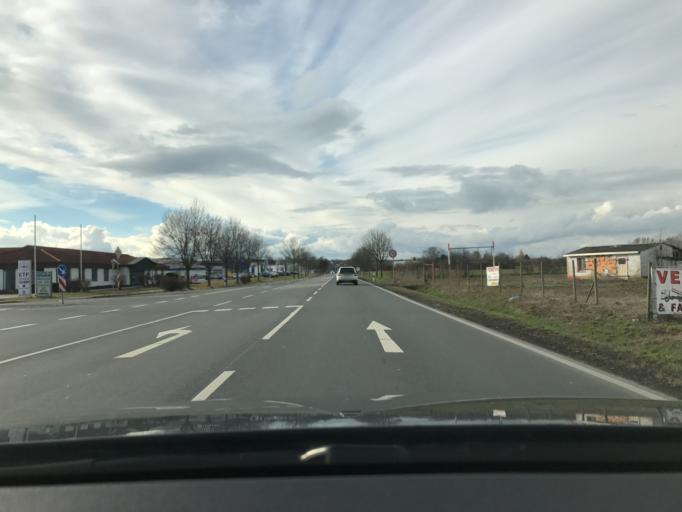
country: DE
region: Saxony-Anhalt
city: Erdeborn
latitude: 51.5071
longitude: 11.5913
